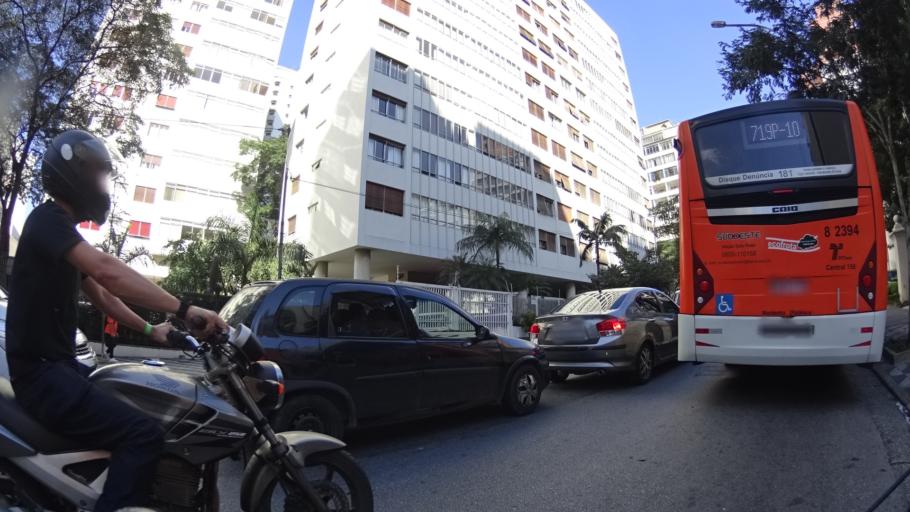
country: BR
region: Sao Paulo
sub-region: Sao Paulo
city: Sao Paulo
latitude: -23.5429
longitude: -46.6563
